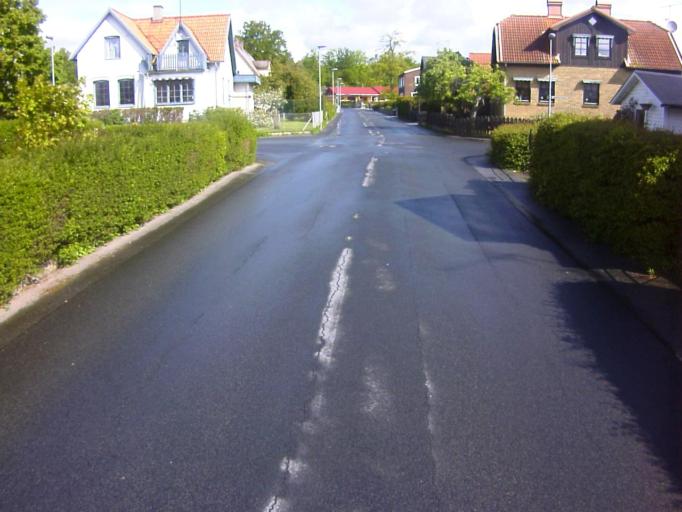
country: SE
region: Blekinge
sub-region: Solvesborgs Kommun
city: Soelvesborg
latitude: 56.0531
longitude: 14.5749
